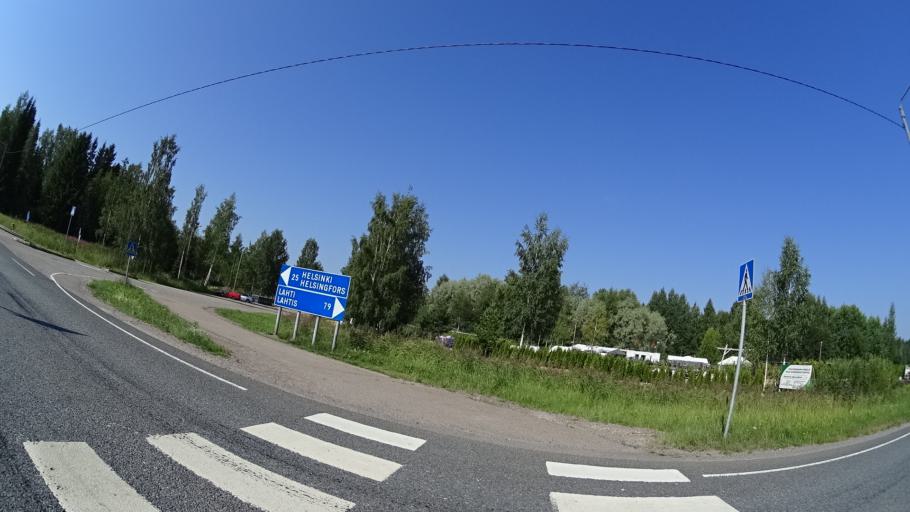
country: FI
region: Uusimaa
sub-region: Helsinki
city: Kerava
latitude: 60.3468
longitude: 25.1270
